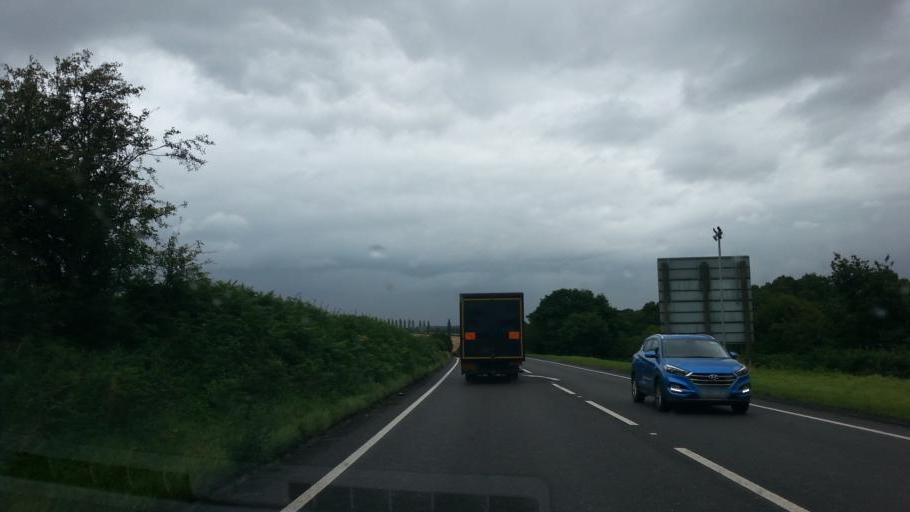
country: GB
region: England
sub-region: Nottinghamshire
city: Bilsthorpe
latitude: 53.1219
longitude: -1.0606
